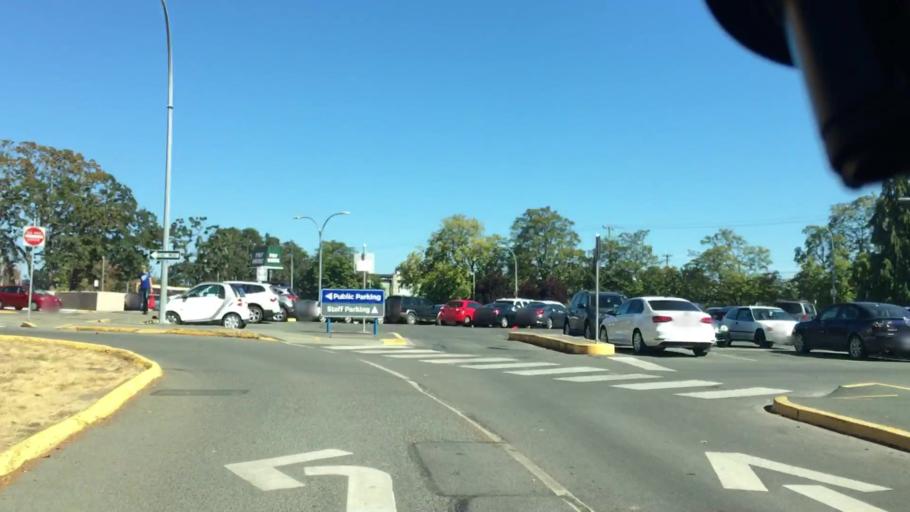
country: CA
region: British Columbia
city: Oak Bay
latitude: 48.4315
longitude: -123.3287
